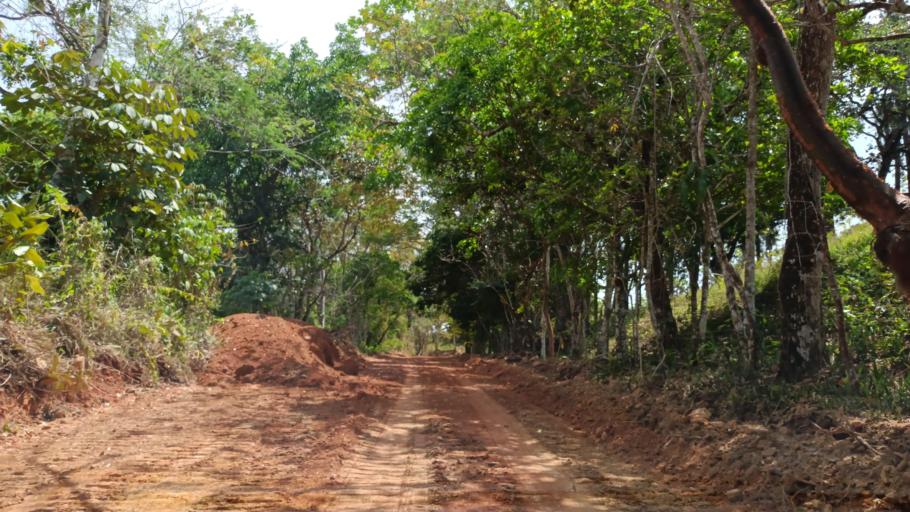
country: PA
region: Panama
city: La Cabima
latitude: 9.1227
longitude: -79.4955
